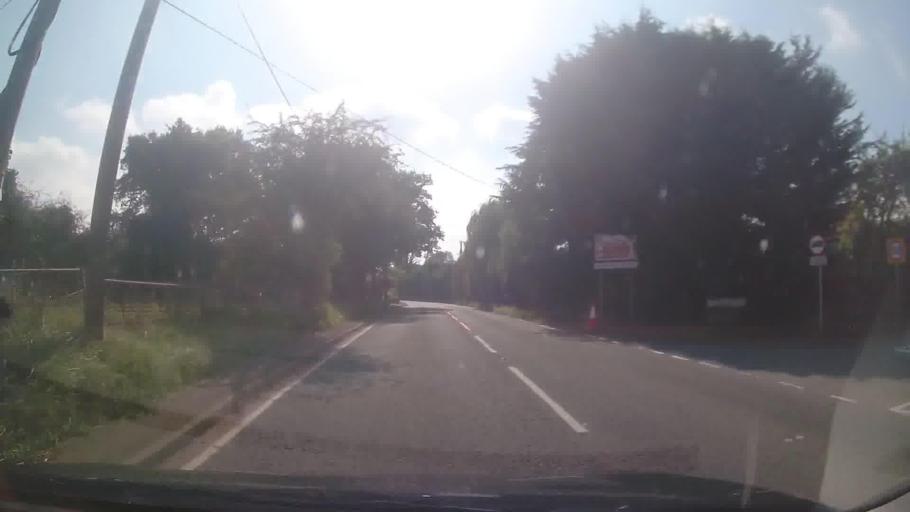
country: GB
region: England
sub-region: Cheshire West and Chester
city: Beeston
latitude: 53.1085
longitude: -2.6611
